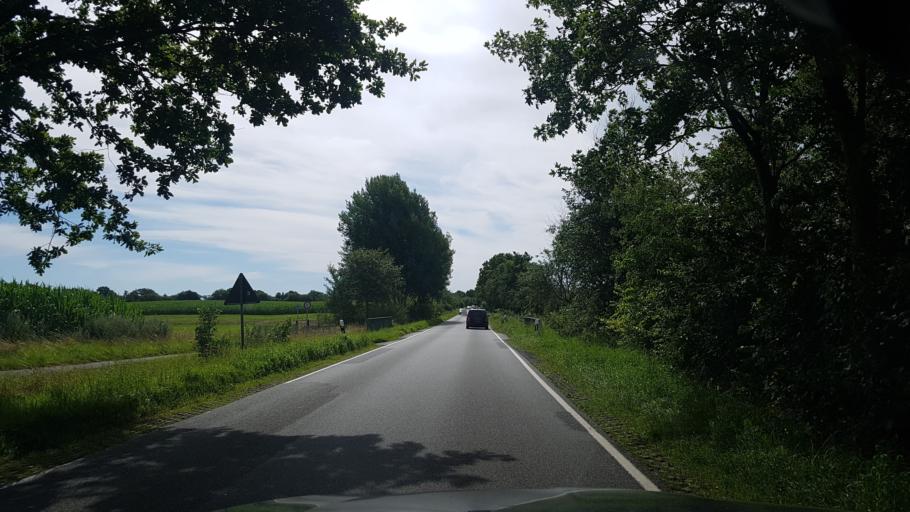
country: DE
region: Schleswig-Holstein
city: Handewitt
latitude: 54.7874
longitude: 9.3220
